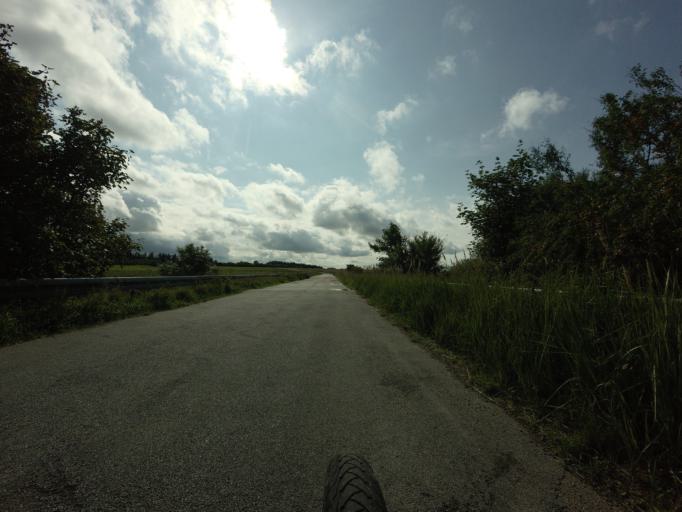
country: DK
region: North Denmark
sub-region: Hjorring Kommune
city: Hirtshals
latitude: 57.5506
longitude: 10.0594
